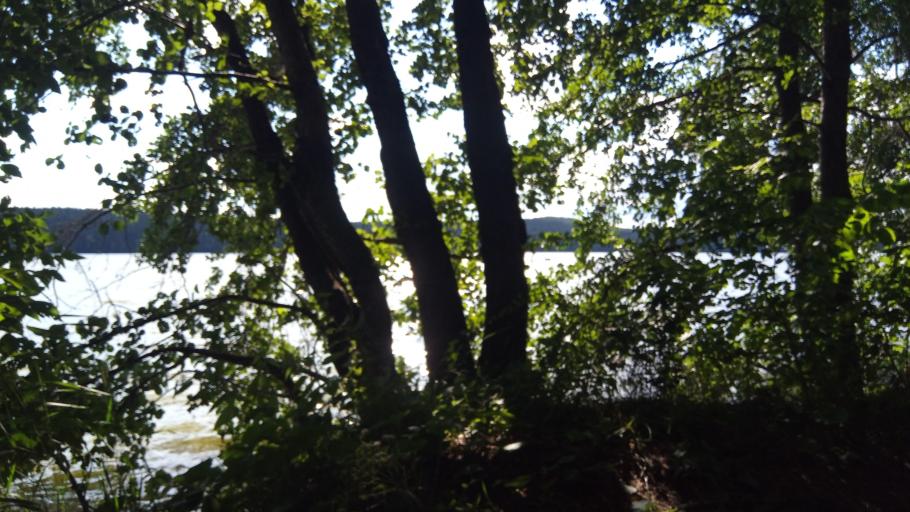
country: RU
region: Chelyabinsk
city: Chebarkul'
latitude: 55.0167
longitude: 60.3121
